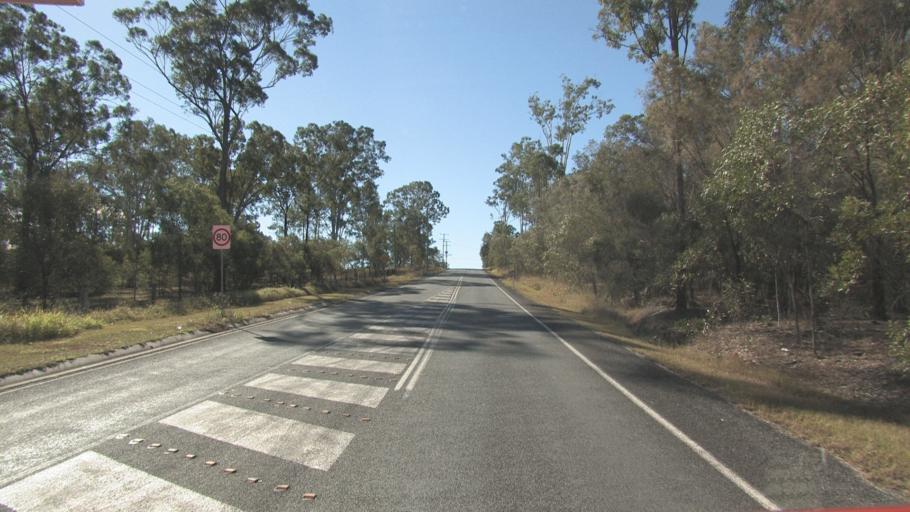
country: AU
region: Queensland
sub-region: Logan
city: Cedar Vale
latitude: -27.8328
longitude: 153.0526
